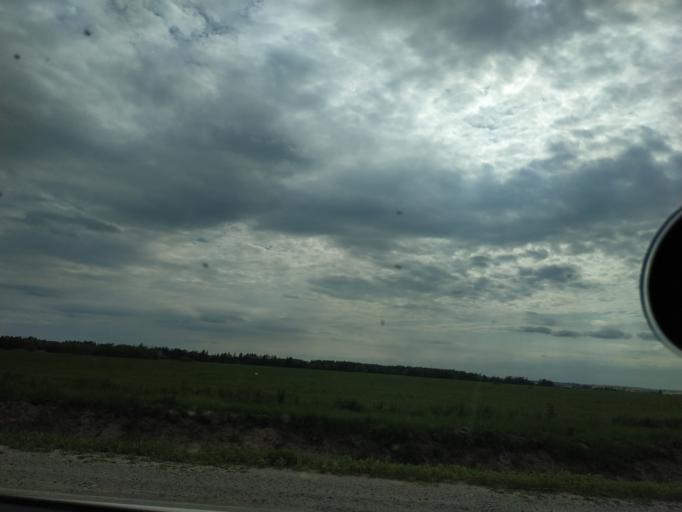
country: RU
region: Moskovskaya
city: Malyshevo
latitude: 55.5023
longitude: 38.2968
